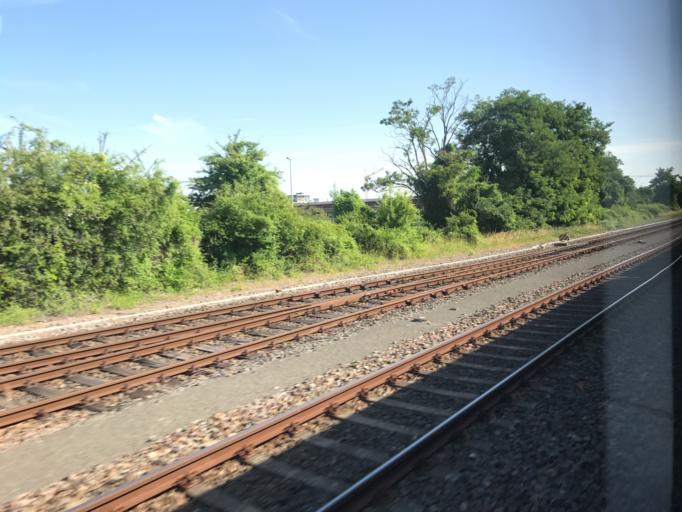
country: DE
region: Rheinland-Pfalz
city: Bad Kreuznach
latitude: 49.8480
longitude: 7.8758
